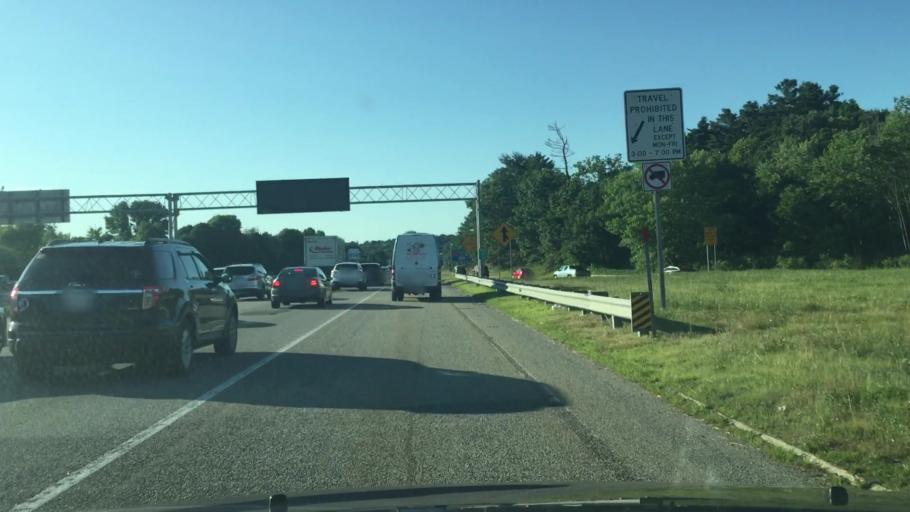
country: US
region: Massachusetts
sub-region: Essex County
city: Methuen
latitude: 42.6924
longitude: -71.2070
